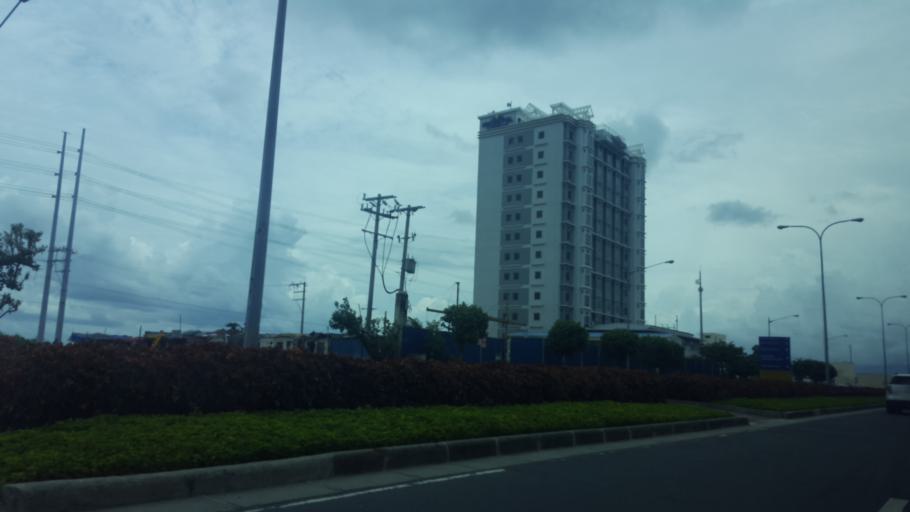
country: PH
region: Metro Manila
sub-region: City of Manila
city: Port Area
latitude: 14.5310
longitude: 120.9811
